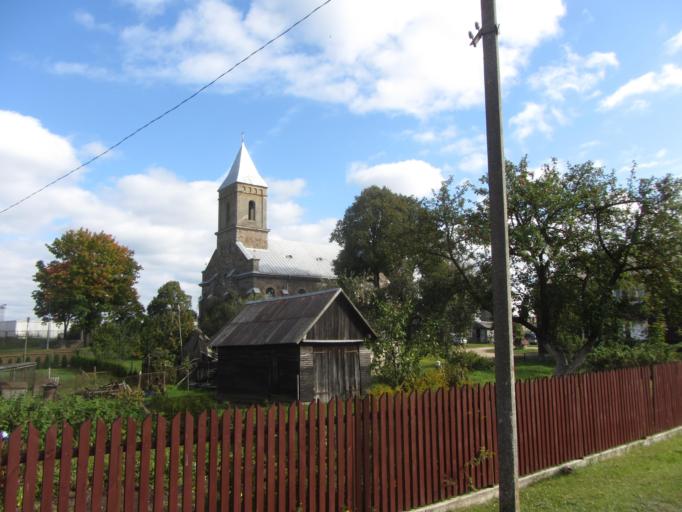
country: LT
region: Vilnius County
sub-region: Trakai
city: Rudiskes
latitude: 54.5134
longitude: 24.8236
